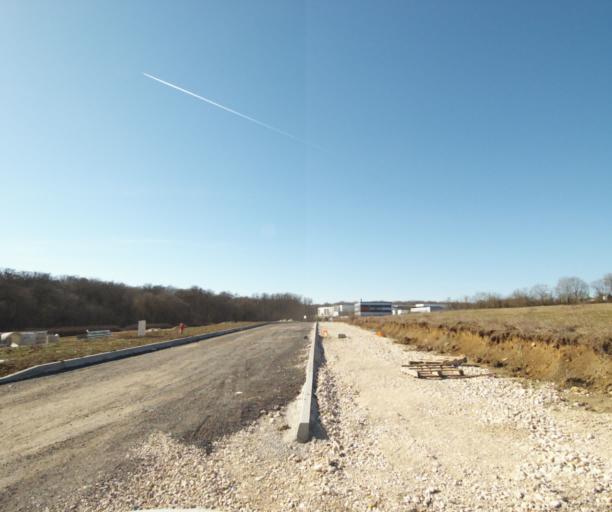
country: FR
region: Lorraine
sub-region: Departement de Meurthe-et-Moselle
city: Fleville-devant-Nancy
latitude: 48.6078
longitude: 6.1999
